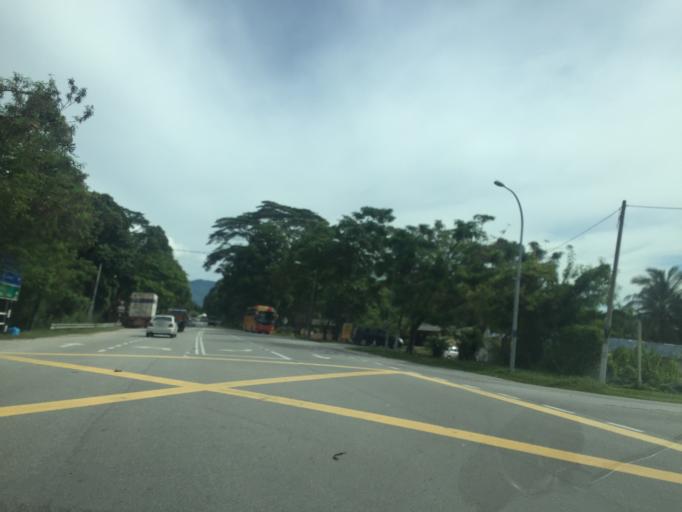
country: MY
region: Negeri Sembilan
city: Seremban
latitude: 2.7304
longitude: 101.9621
